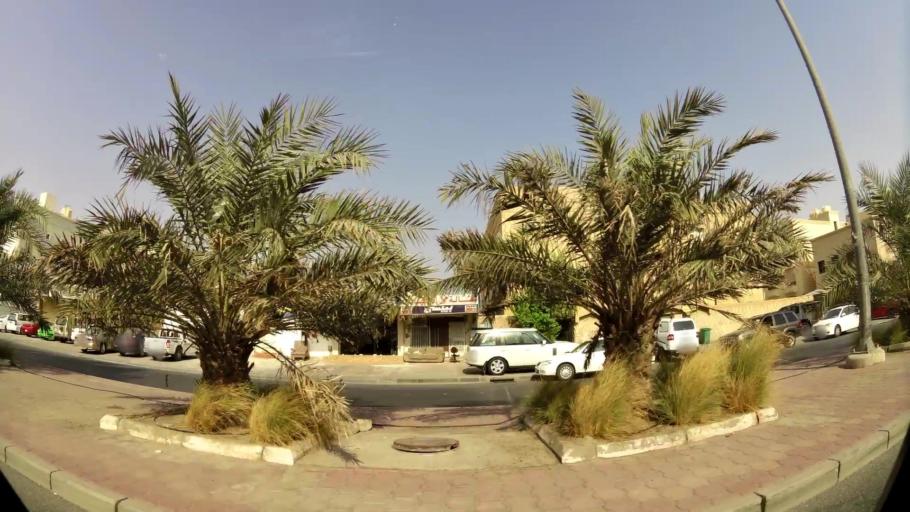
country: KW
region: Muhafazat al Jahra'
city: Al Jahra'
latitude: 29.3529
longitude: 47.6790
